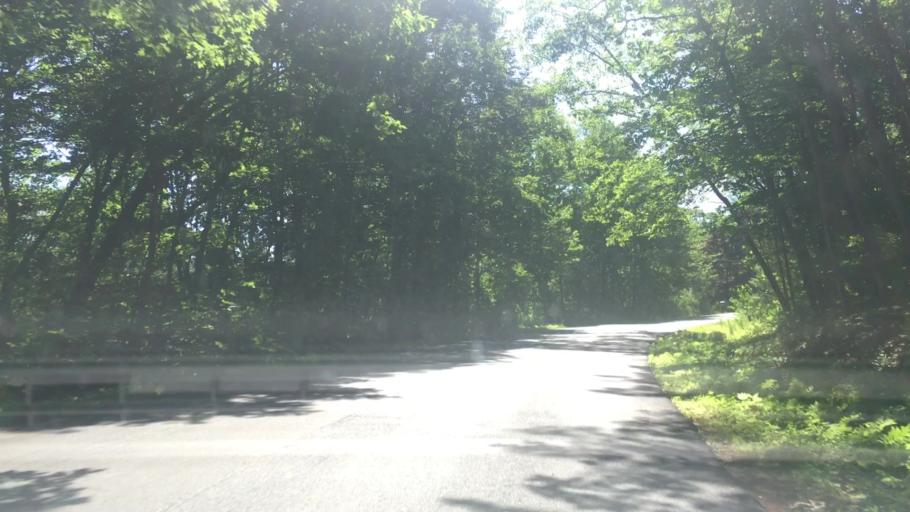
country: US
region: Maine
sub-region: Waldo County
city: Northport
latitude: 44.3812
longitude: -68.9723
